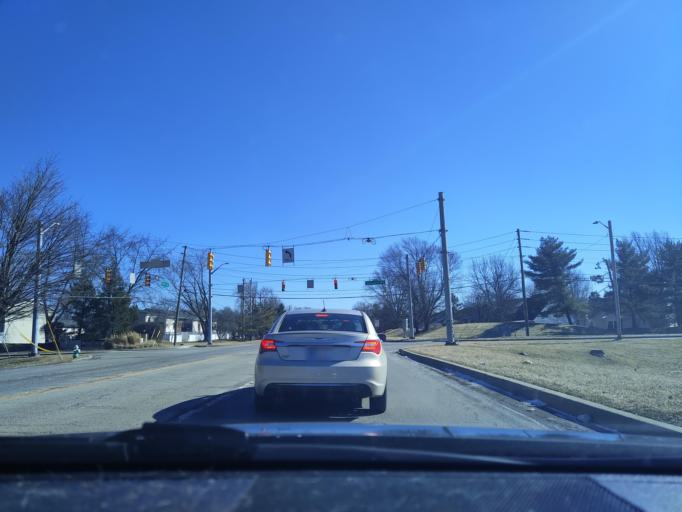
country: US
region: Indiana
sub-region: Marion County
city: Meridian Hills
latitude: 39.8974
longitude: -86.1940
